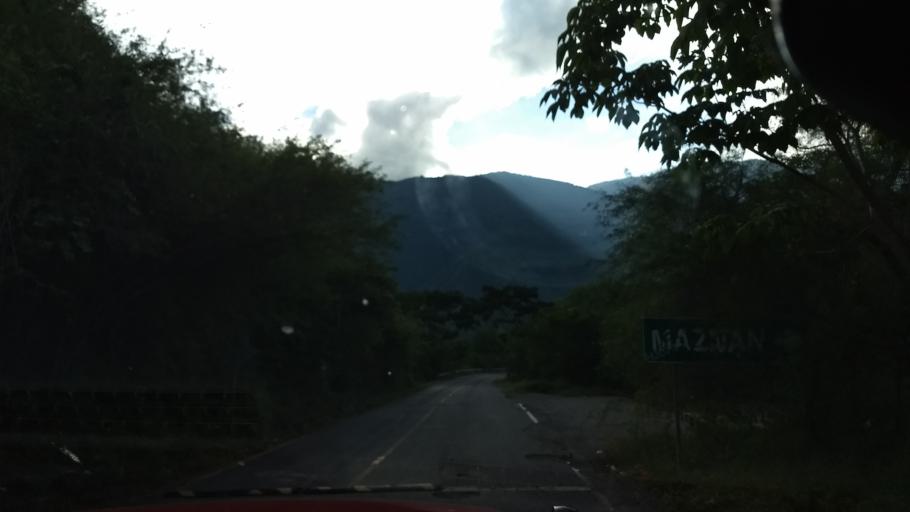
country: MX
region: Colima
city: Suchitlan
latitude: 19.4552
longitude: -103.8242
